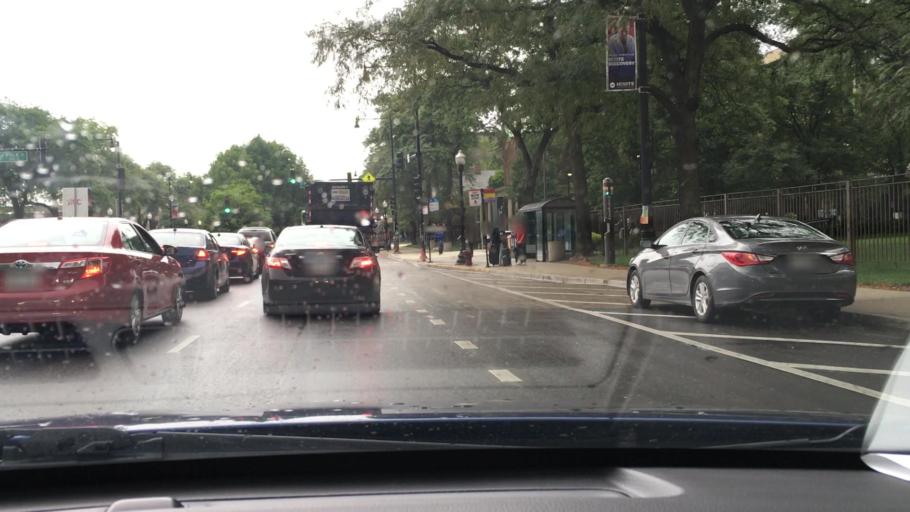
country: US
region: Illinois
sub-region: Cook County
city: Chicago
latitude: 41.8724
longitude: -87.6471
